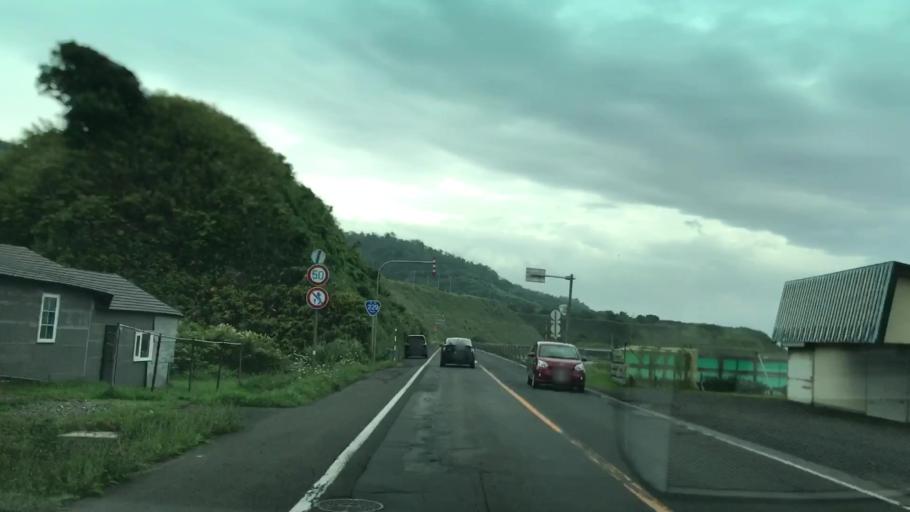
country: JP
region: Hokkaido
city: Iwanai
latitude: 42.8428
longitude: 140.3251
